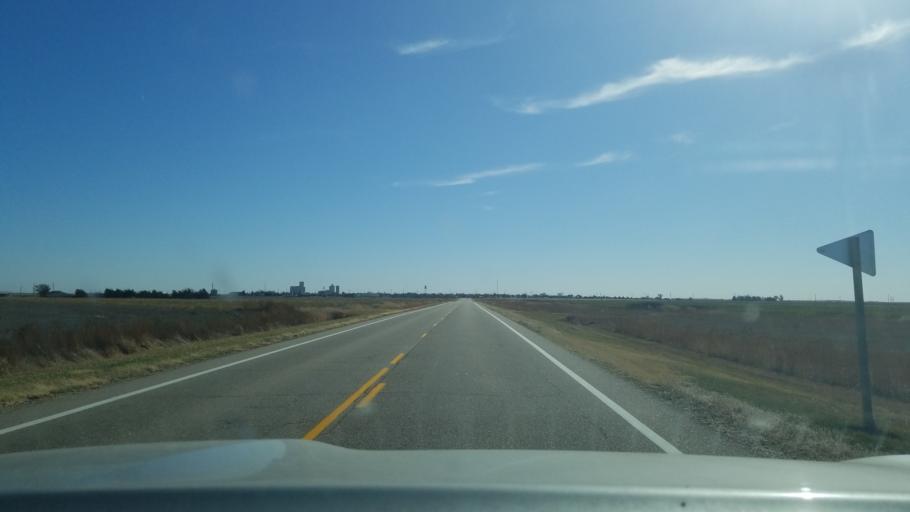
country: US
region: Kansas
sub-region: Kiowa County
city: Greensburg
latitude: 37.5644
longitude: -99.6554
